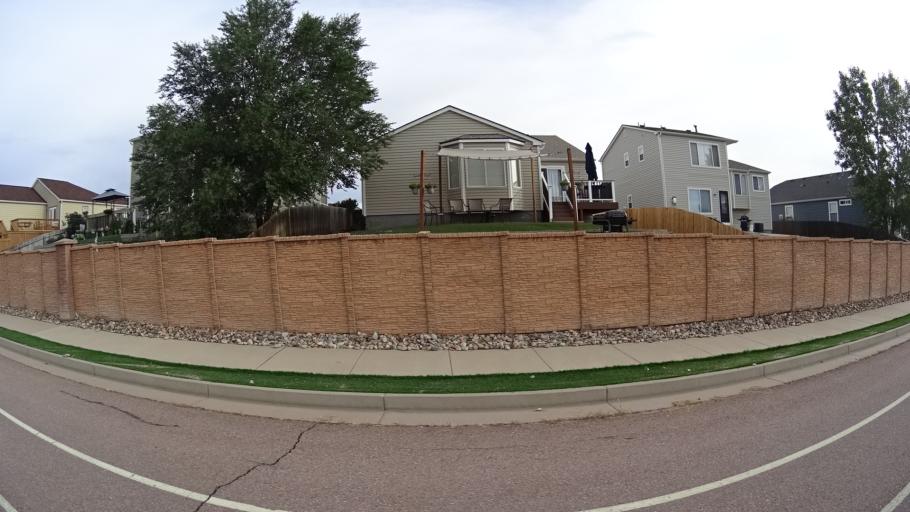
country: US
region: Colorado
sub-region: El Paso County
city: Fountain
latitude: 38.7147
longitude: -104.6894
